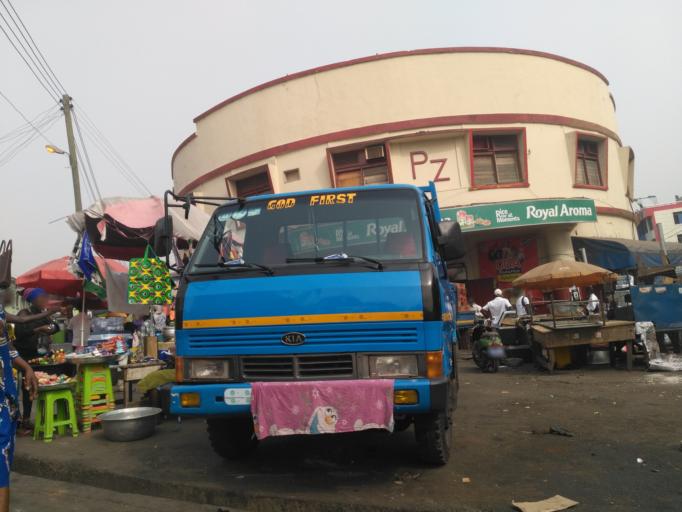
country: GH
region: Ashanti
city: Kumasi
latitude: 6.6959
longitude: -1.6228
